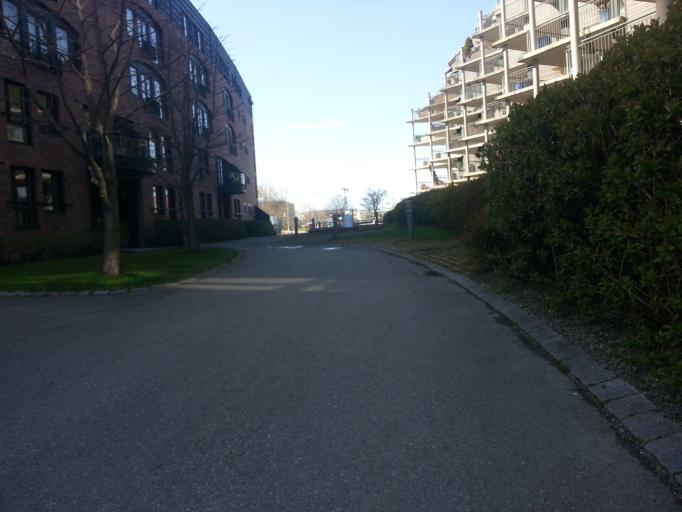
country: NO
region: Sor-Trondelag
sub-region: Trondheim
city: Trondheim
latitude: 63.4340
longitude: 10.4094
